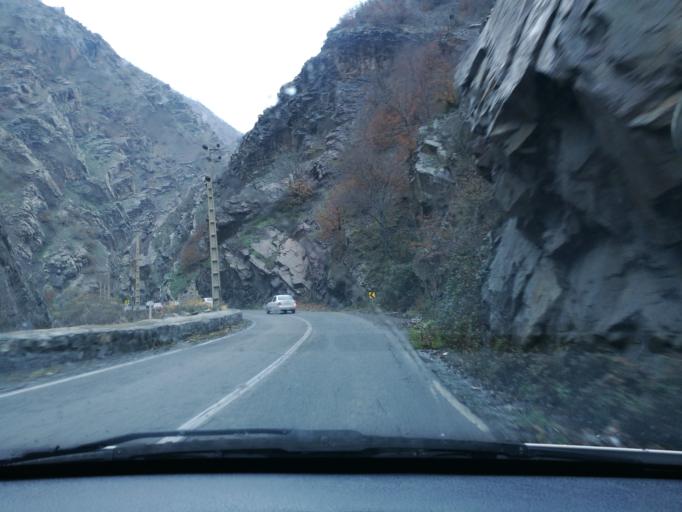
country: IR
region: Mazandaran
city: Chalus
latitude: 36.2779
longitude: 51.2442
